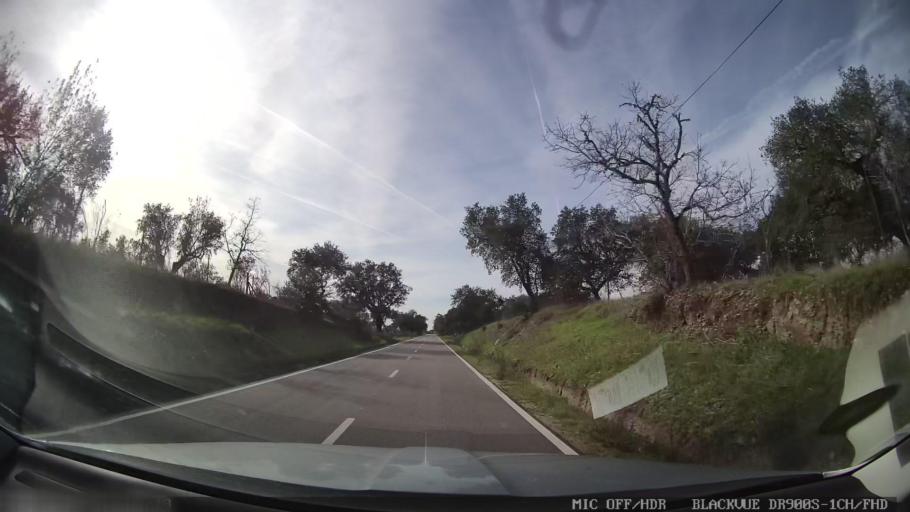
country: PT
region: Portalegre
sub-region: Nisa
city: Nisa
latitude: 39.4523
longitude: -7.7120
